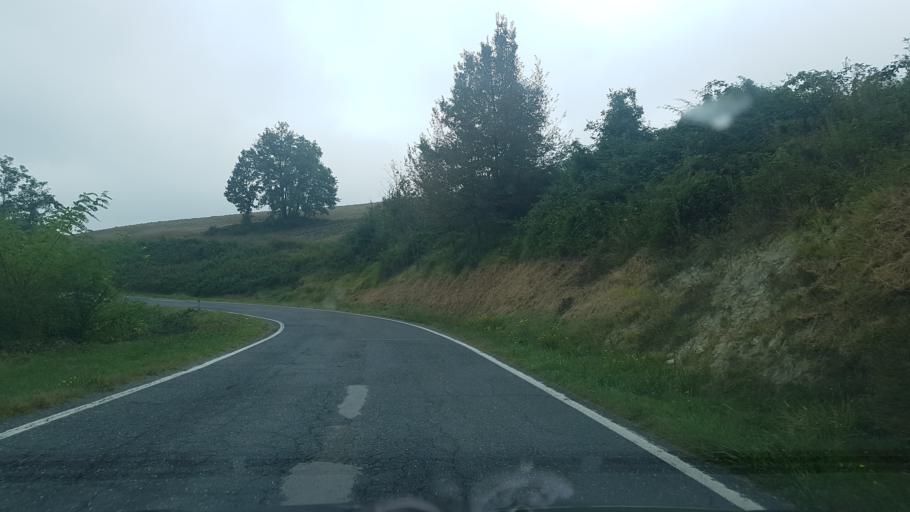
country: IT
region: Piedmont
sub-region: Provincia di Cuneo
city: Paroldo
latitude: 44.4288
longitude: 8.0888
